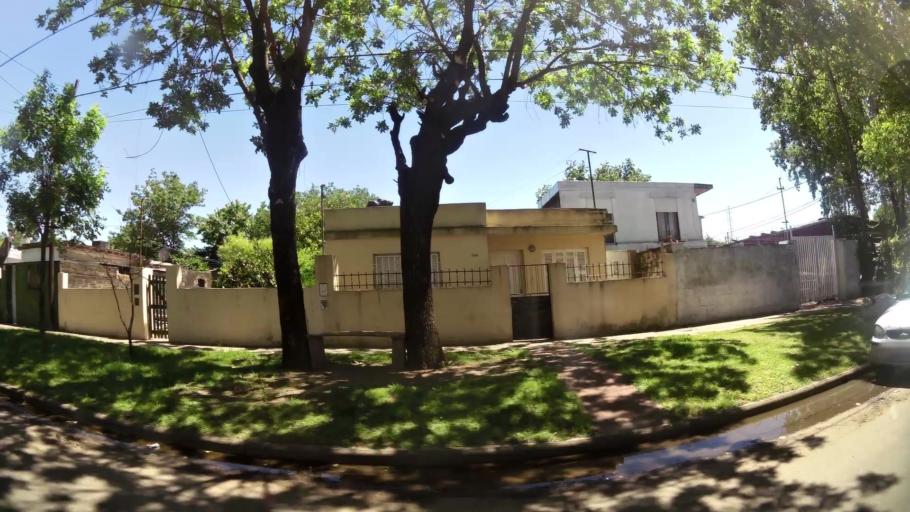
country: AR
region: Santa Fe
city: Perez
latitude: -32.9469
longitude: -60.7196
